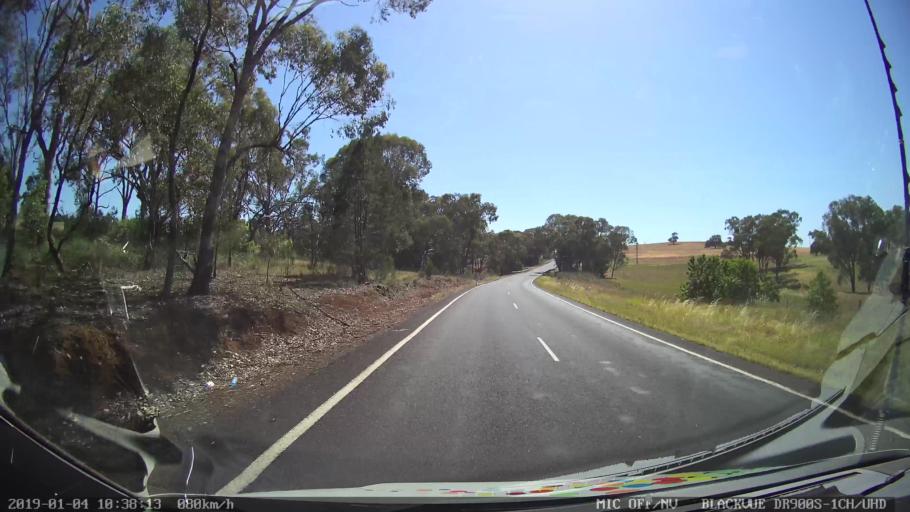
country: AU
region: New South Wales
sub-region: Cabonne
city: Molong
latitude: -33.2935
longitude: 148.7057
